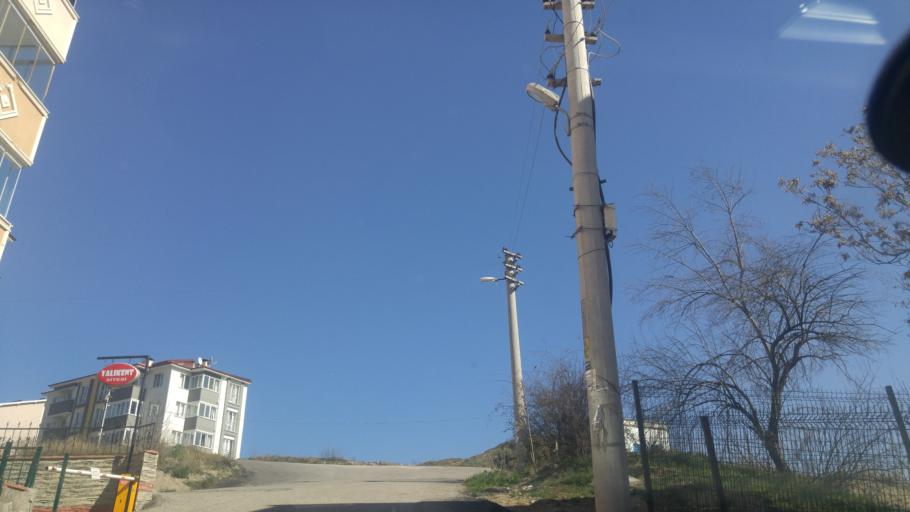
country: TR
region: Karabuk
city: Safranbolu
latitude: 41.2237
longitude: 32.6649
